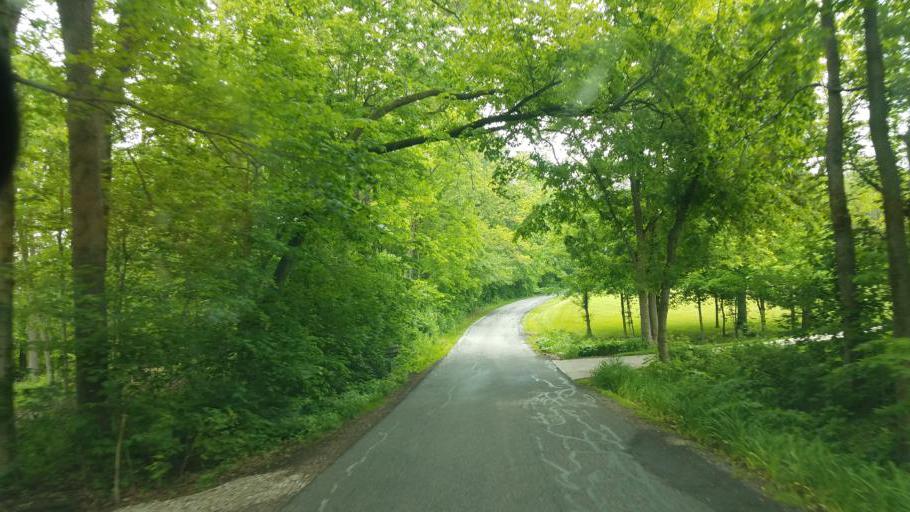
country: US
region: Ohio
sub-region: Delaware County
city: Delaware
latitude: 40.3170
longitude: -83.1683
